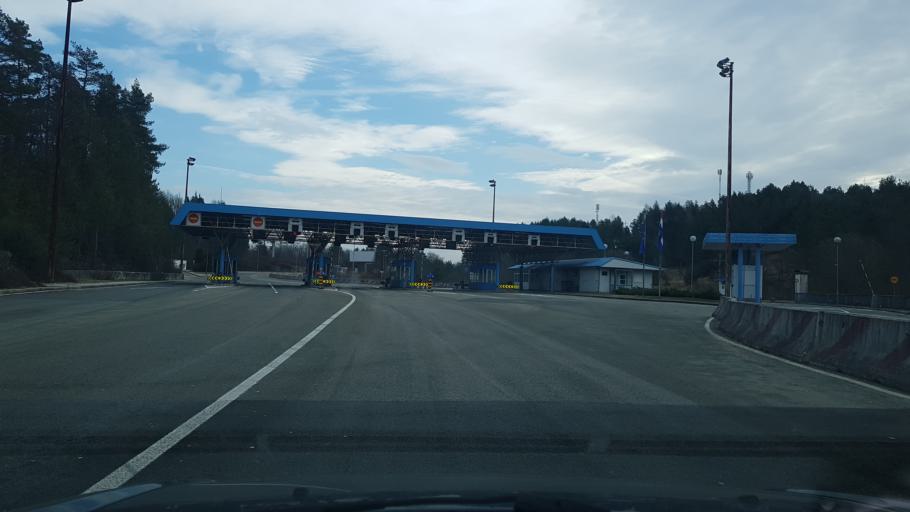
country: SI
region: Ilirska Bistrica
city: Ilirska Bistrica
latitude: 45.4919
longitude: 14.2146
